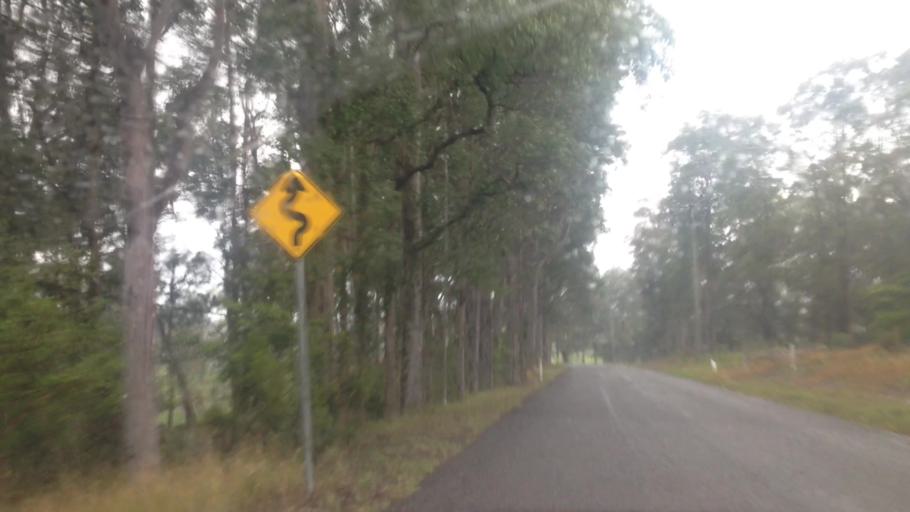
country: AU
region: New South Wales
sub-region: Wyong Shire
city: Little Jilliby
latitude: -33.2127
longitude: 151.3713
